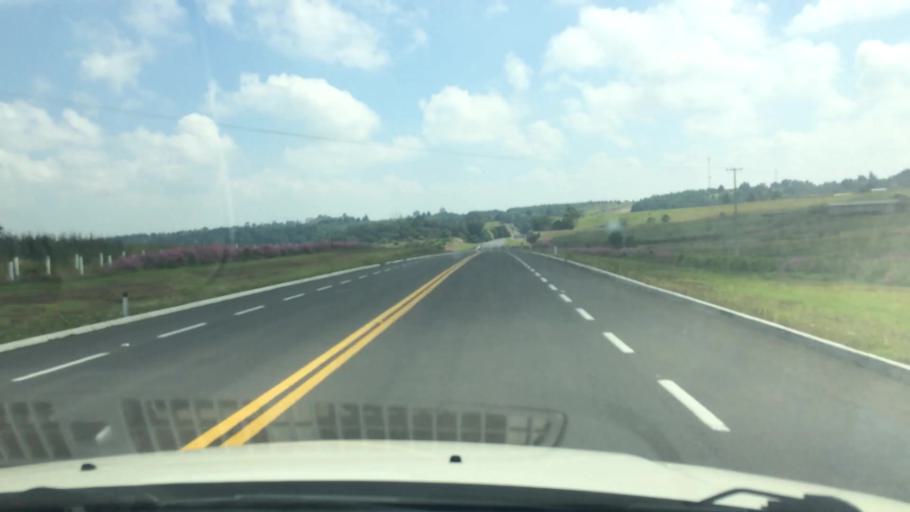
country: MX
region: Mexico
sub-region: Villa Victoria
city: Colonia Doctor Gustavo Baz
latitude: 19.3741
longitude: -99.9122
